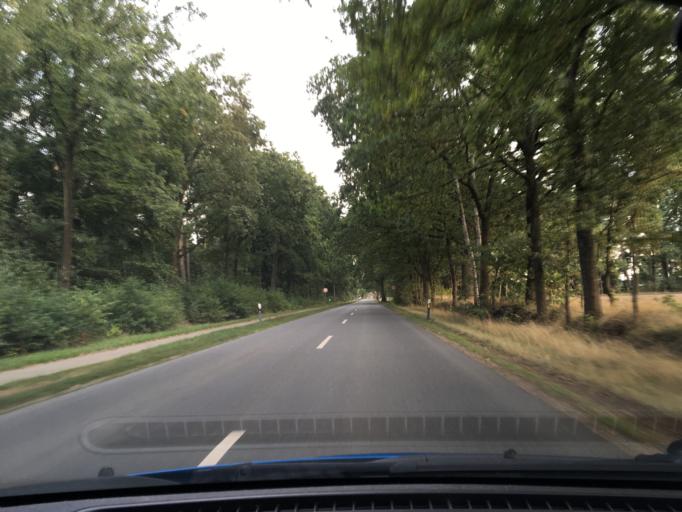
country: DE
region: Lower Saxony
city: Westergellersen
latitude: 53.2428
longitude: 10.2361
